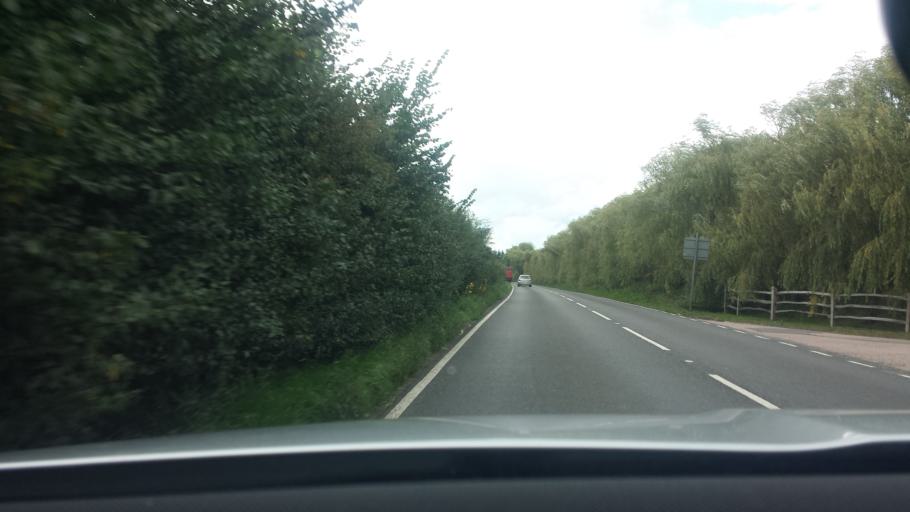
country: GB
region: England
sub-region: Kent
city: Staplehurst
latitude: 51.1910
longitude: 0.5421
